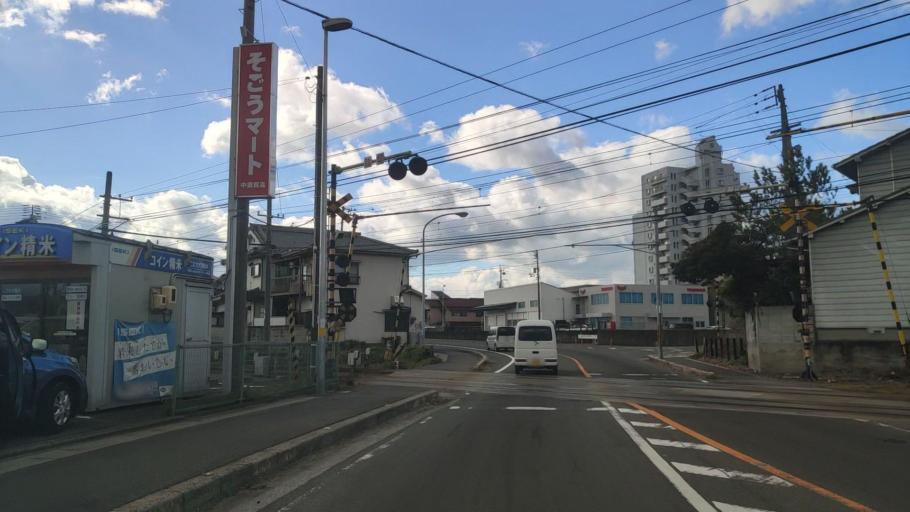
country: JP
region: Ehime
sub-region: Shikoku-chuo Shi
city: Matsuyama
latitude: 33.8654
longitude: 132.7193
